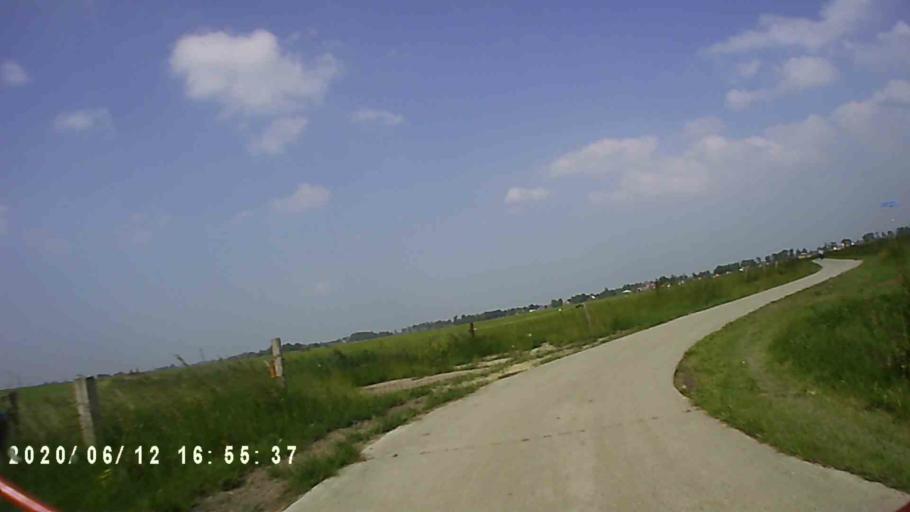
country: NL
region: Groningen
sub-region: Gemeente Groningen
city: Korrewegwijk
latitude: 53.2650
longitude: 6.5512
